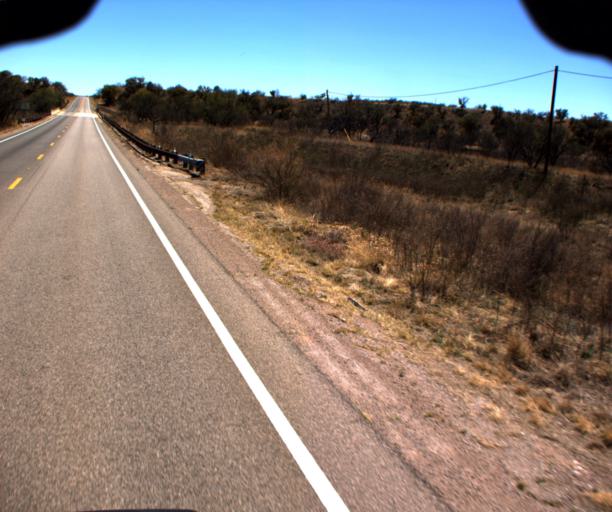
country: US
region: Arizona
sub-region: Pima County
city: Corona de Tucson
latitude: 31.7374
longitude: -110.6634
